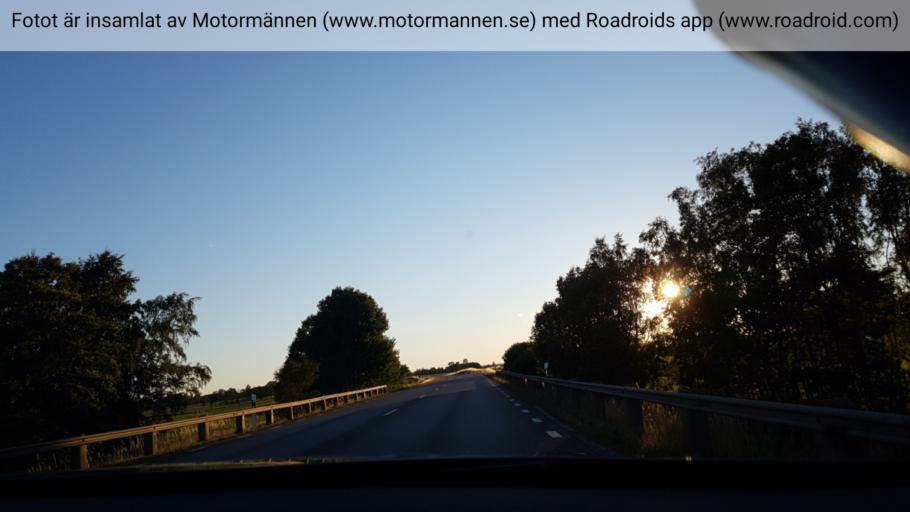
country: SE
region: Vaestra Goetaland
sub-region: Tibro Kommun
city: Tibro
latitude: 58.3508
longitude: 14.0860
